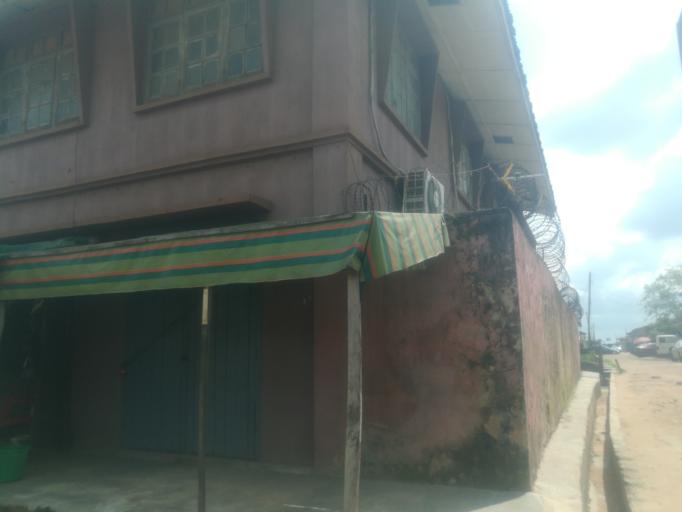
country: NG
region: Oyo
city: Ibadan
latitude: 7.3656
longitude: 3.8779
